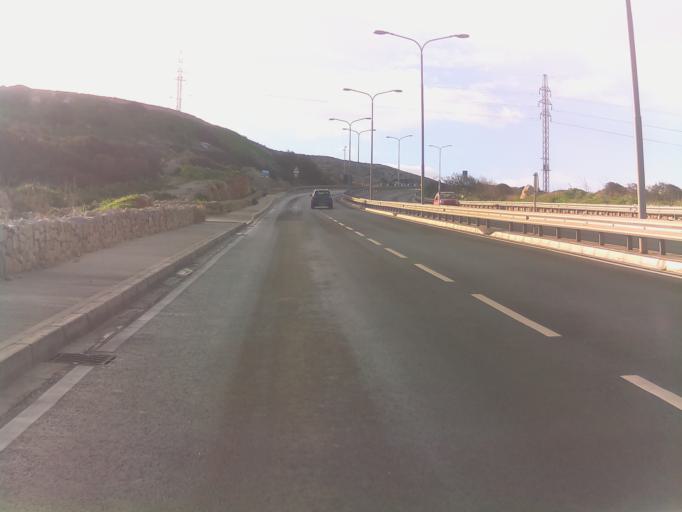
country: MT
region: Il-Mellieha
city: Mellieha
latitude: 35.9594
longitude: 14.3509
